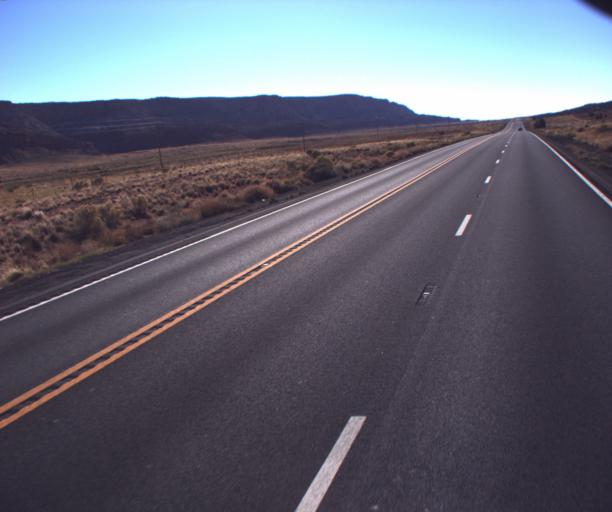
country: US
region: Arizona
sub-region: Coconino County
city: LeChee
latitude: 36.4597
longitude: -111.5652
